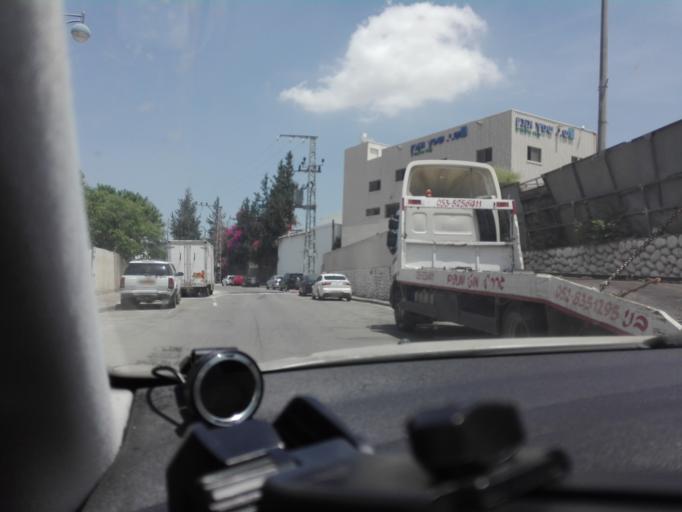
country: IL
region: Central District
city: Bene 'Ayish
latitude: 31.7341
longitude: 34.7528
